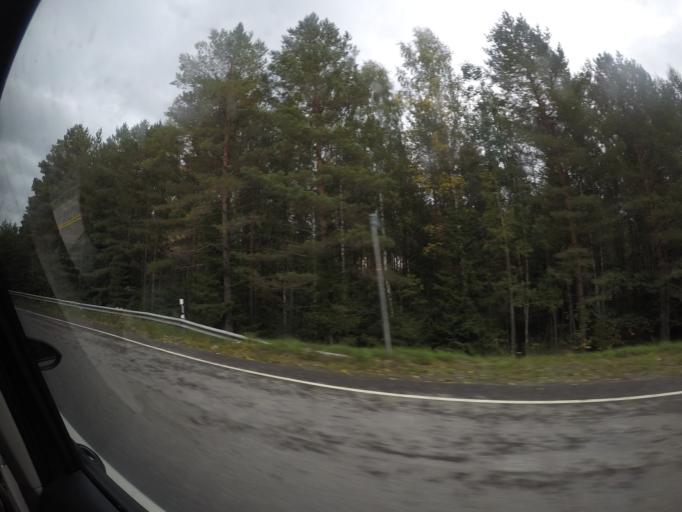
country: FI
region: Haeme
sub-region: Haemeenlinna
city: Parola
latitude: 61.1629
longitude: 24.4110
